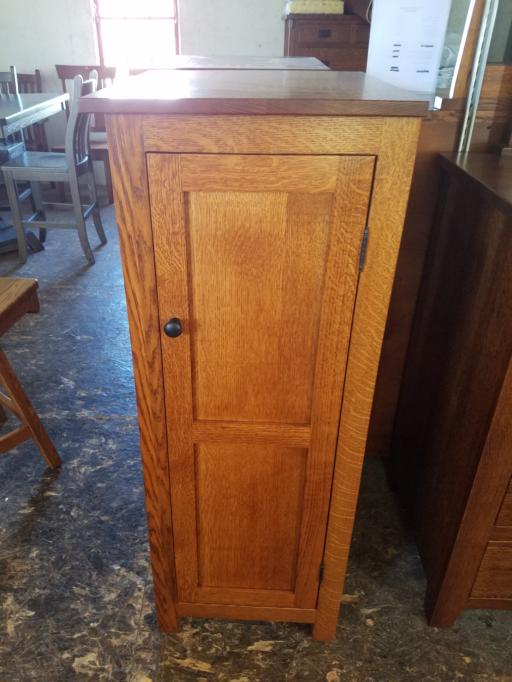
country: US
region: Iowa
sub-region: Decatur County
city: Lamoni
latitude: 40.6241
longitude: -93.8643
